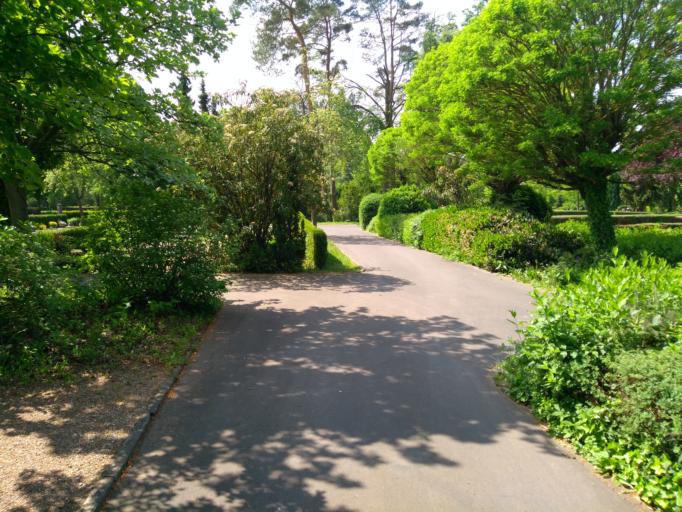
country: DE
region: Bavaria
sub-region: Regierungsbezirk Unterfranken
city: Bad Kissingen
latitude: 50.2090
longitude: 10.0904
